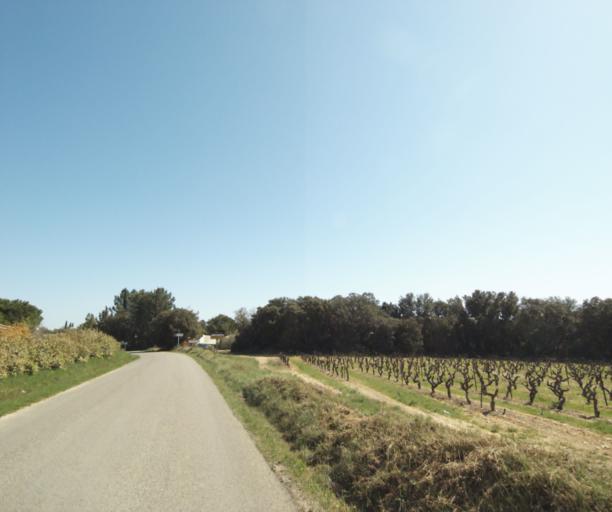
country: FR
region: Languedoc-Roussillon
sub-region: Departement de l'Herault
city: Sussargues
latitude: 43.7159
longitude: 3.9946
